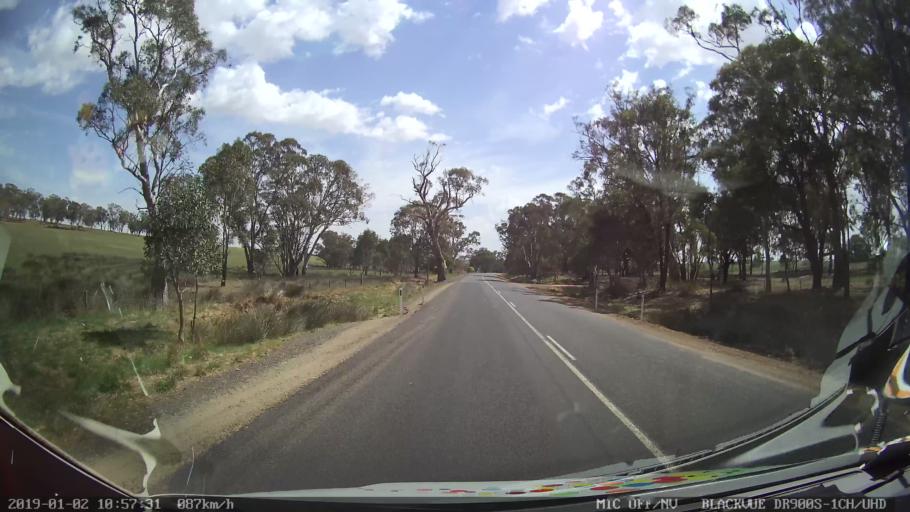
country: AU
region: New South Wales
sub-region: Cootamundra
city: Cootamundra
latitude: -34.6343
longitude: 148.2832
